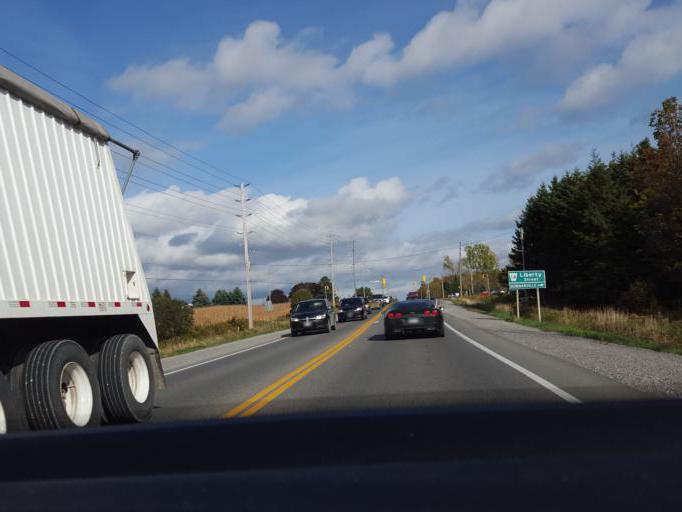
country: CA
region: Ontario
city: Oshawa
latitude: 43.9718
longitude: -78.7106
